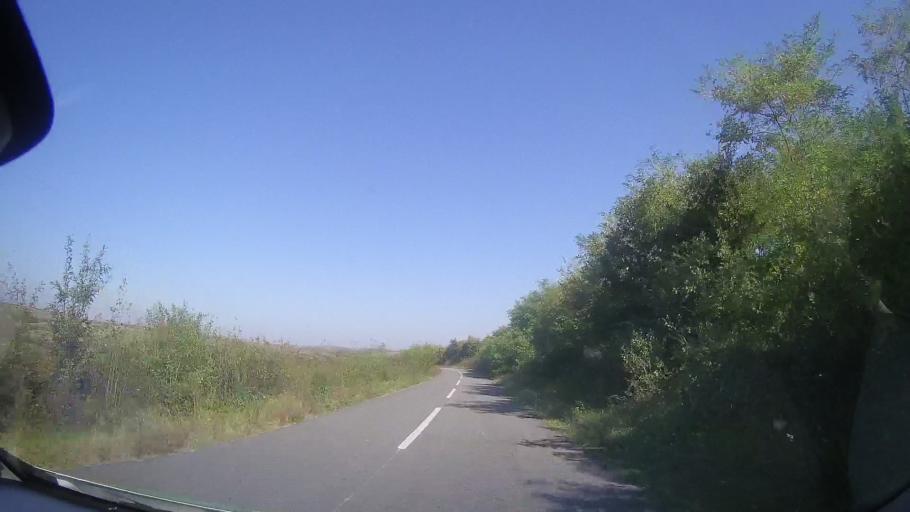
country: RO
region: Timis
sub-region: Comuna Balint
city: Balint
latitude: 45.8310
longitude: 21.8549
